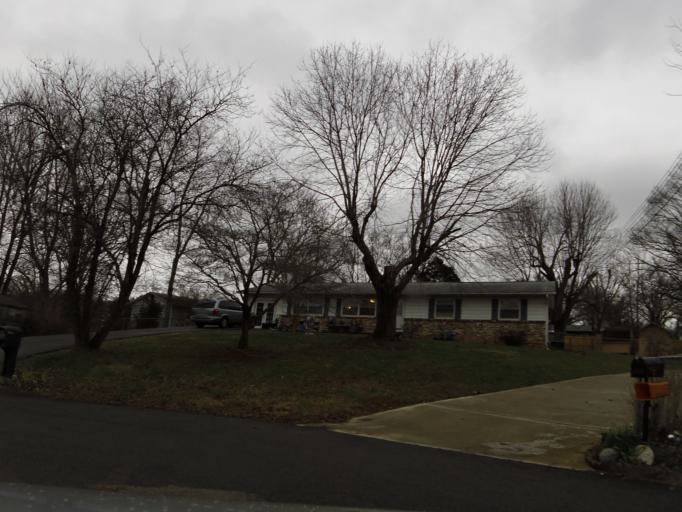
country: US
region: Tennessee
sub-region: Knox County
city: Knoxville
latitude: 35.9786
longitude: -84.0016
